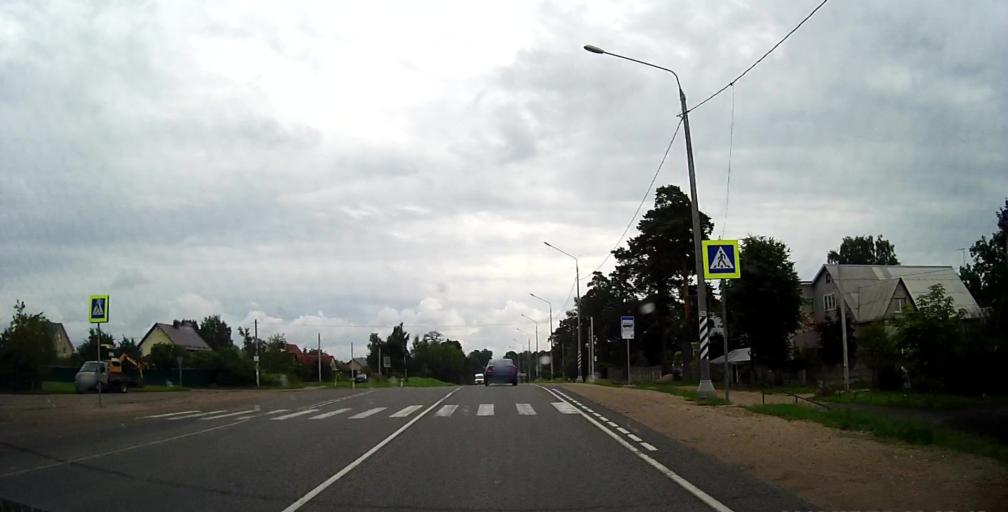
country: RU
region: Smolensk
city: Katyn'
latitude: 54.7843
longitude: 31.8467
